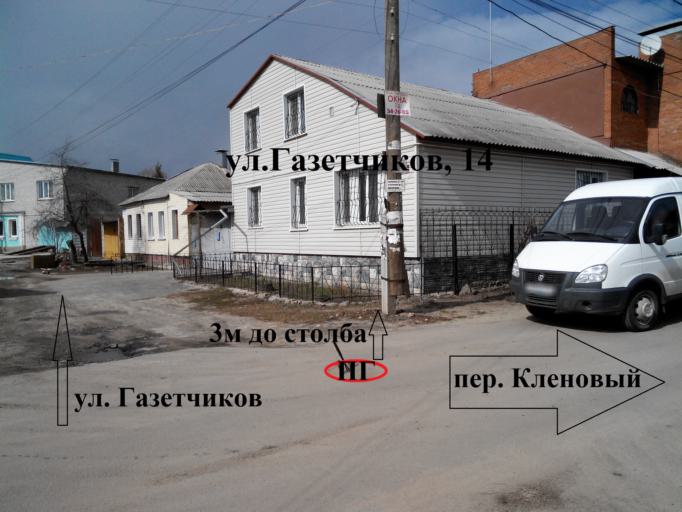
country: RU
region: Voronezj
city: Voronezh
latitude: 51.6351
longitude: 39.1598
